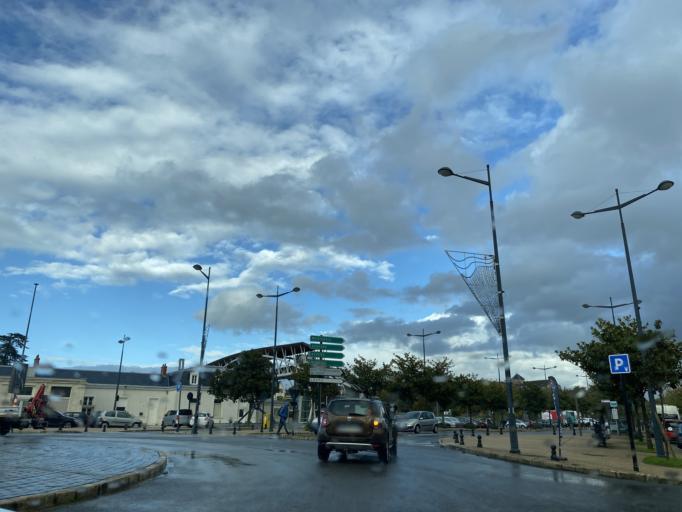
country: FR
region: Centre
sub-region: Departement du Cher
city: Bourges
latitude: 47.0935
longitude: 2.3943
